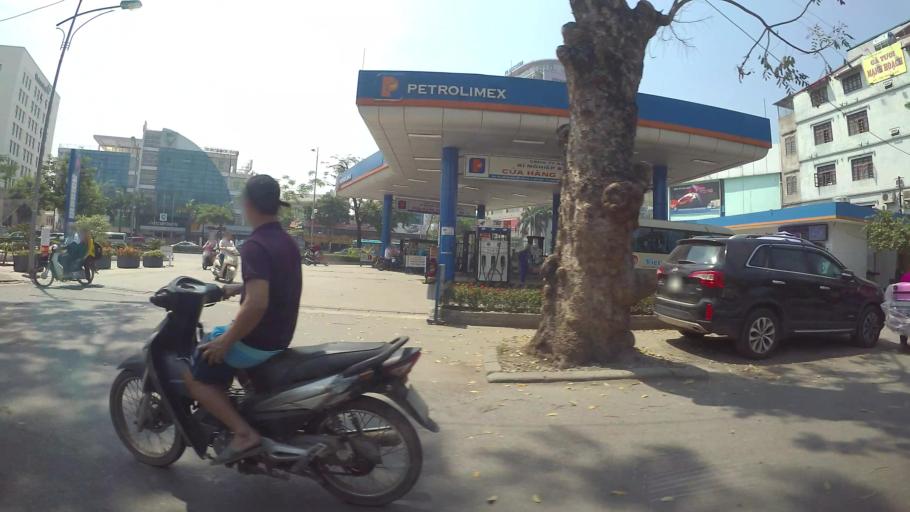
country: VN
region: Ha Noi
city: Hoan Kiem
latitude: 21.0506
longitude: 105.8839
